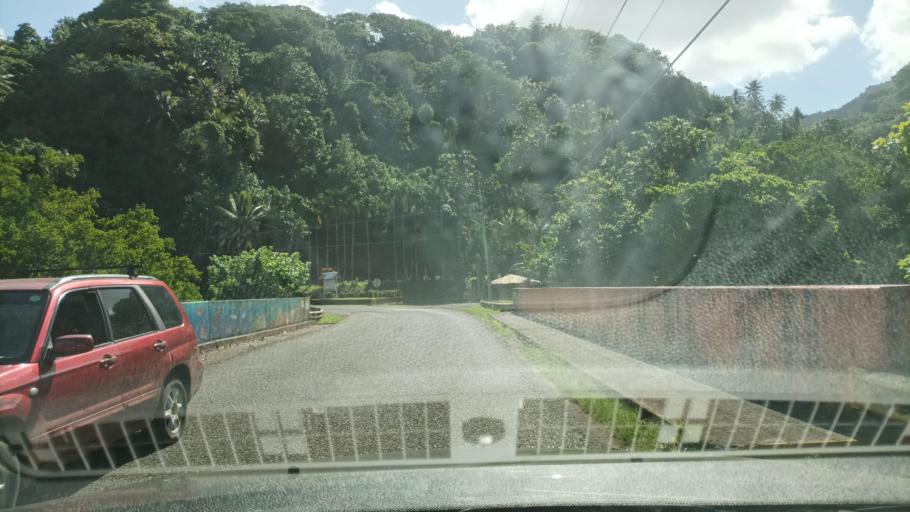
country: FM
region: Kosrae
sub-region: Lelu Municipality
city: Lelu
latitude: 5.3406
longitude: 163.0179
